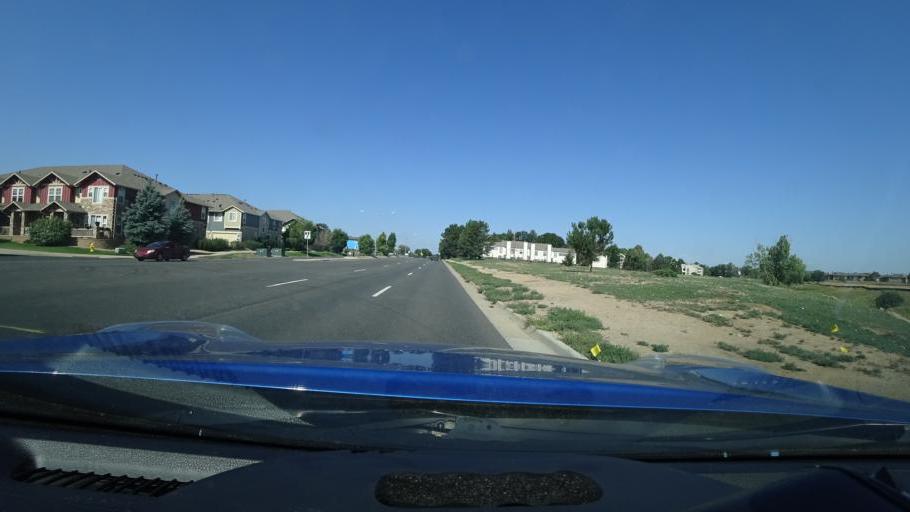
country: US
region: Colorado
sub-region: Adams County
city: Aurora
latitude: 39.7068
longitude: -104.7956
